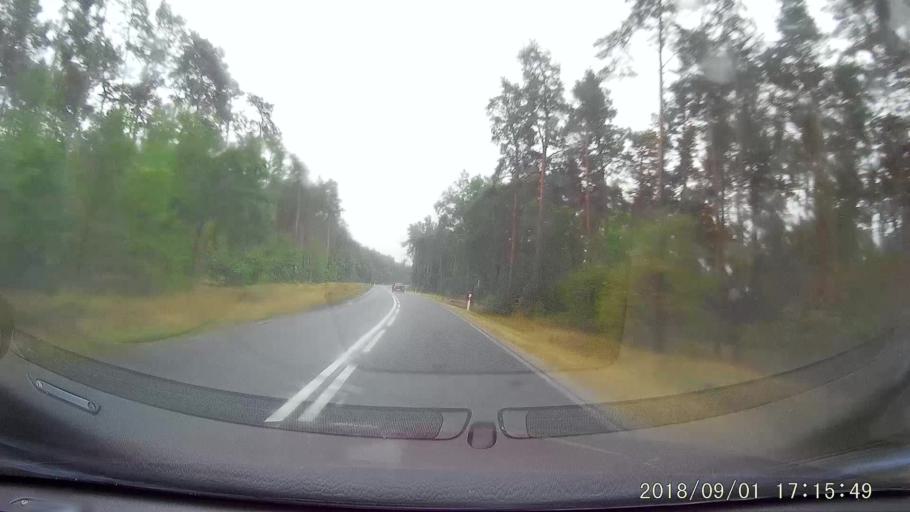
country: PL
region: Lubusz
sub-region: Powiat zielonogorski
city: Nowogrod Bobrzanski
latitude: 51.7706
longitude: 15.2658
